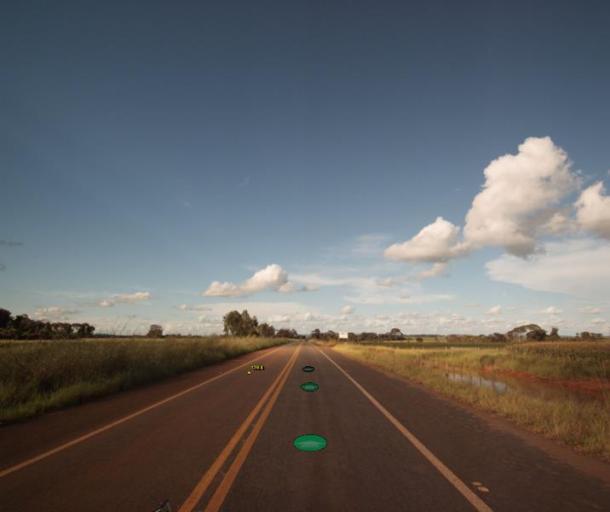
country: BR
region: Goias
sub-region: Itaberai
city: Itaberai
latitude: -15.9839
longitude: -49.6923
